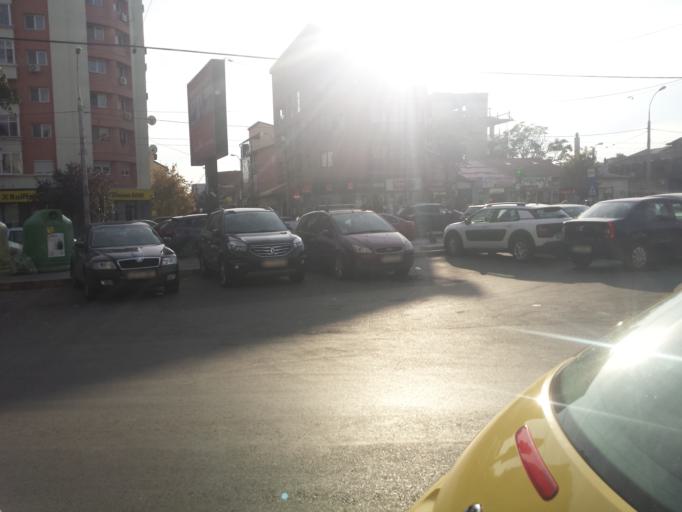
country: RO
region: Bucuresti
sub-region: Municipiul Bucuresti
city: Bucuresti
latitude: 44.4654
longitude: 26.0683
